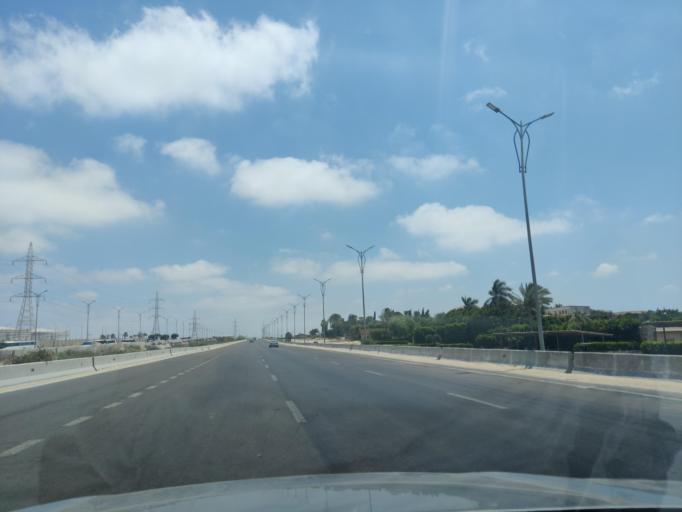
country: EG
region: Alexandria
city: Alexandria
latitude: 31.0166
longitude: 29.7585
